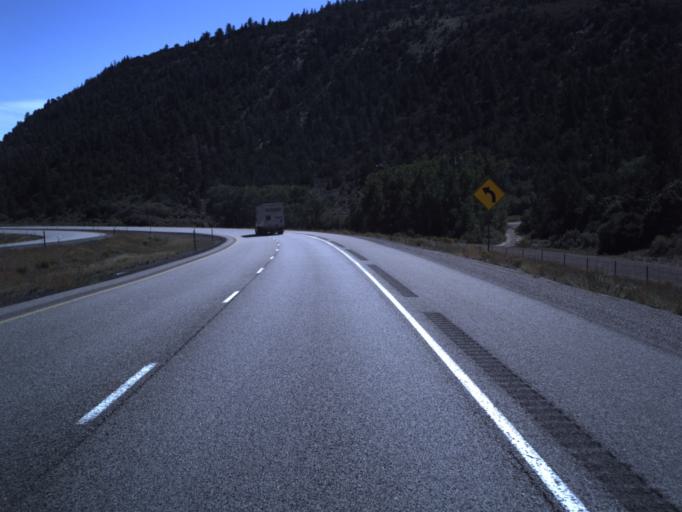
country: US
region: Utah
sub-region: Wayne County
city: Loa
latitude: 38.7570
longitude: -111.4464
